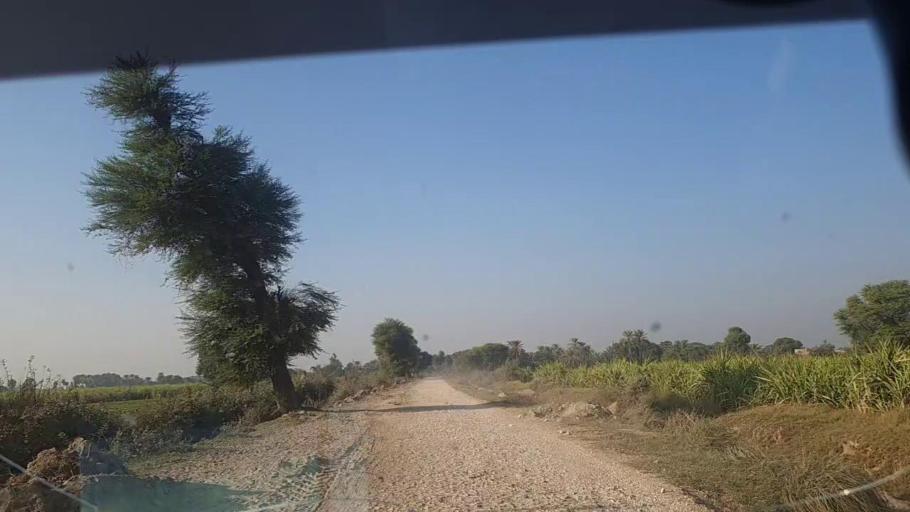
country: PK
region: Sindh
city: Sobhadero
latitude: 27.2648
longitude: 68.3494
